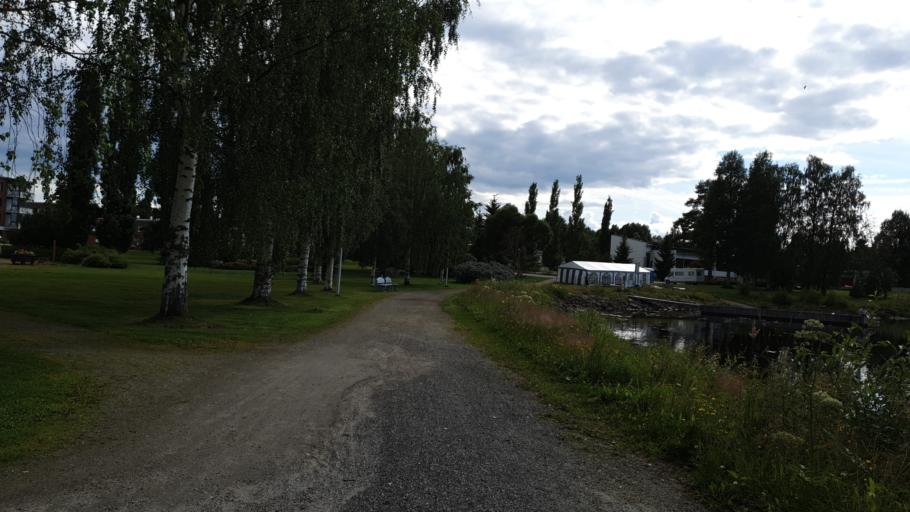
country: FI
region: Kainuu
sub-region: Kehys-Kainuu
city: Kuhmo
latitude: 64.1293
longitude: 29.5162
